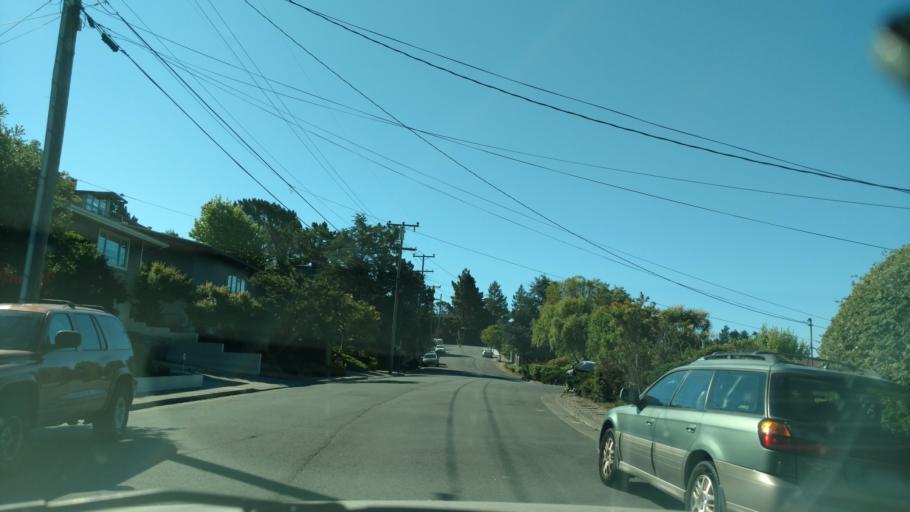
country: US
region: California
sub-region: Contra Costa County
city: Kensington
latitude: 37.9193
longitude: -122.2864
